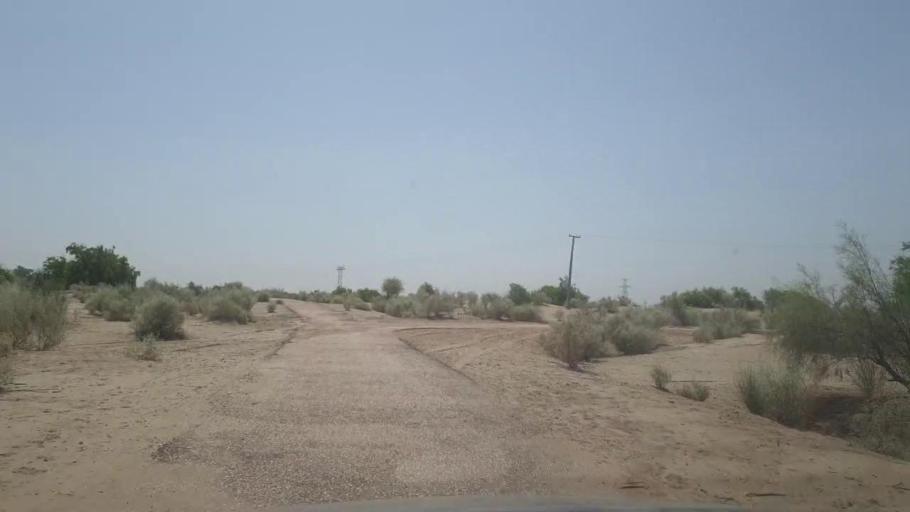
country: PK
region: Sindh
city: Khairpur
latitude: 27.3535
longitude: 69.0783
